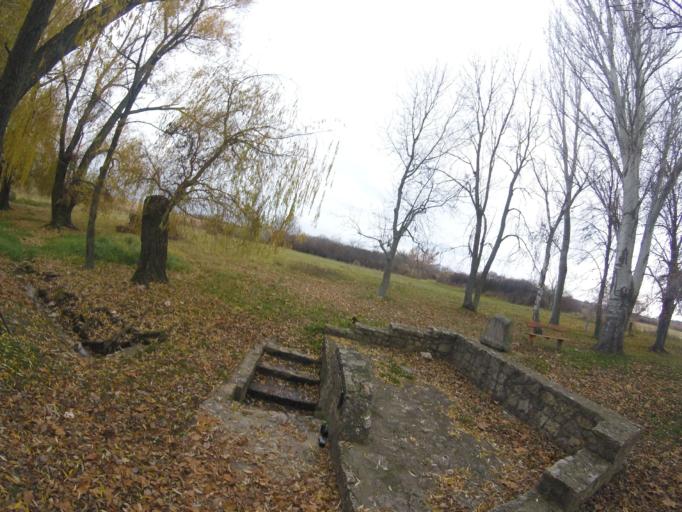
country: HU
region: Veszprem
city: Balatonfured
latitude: 46.9236
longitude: 17.8329
